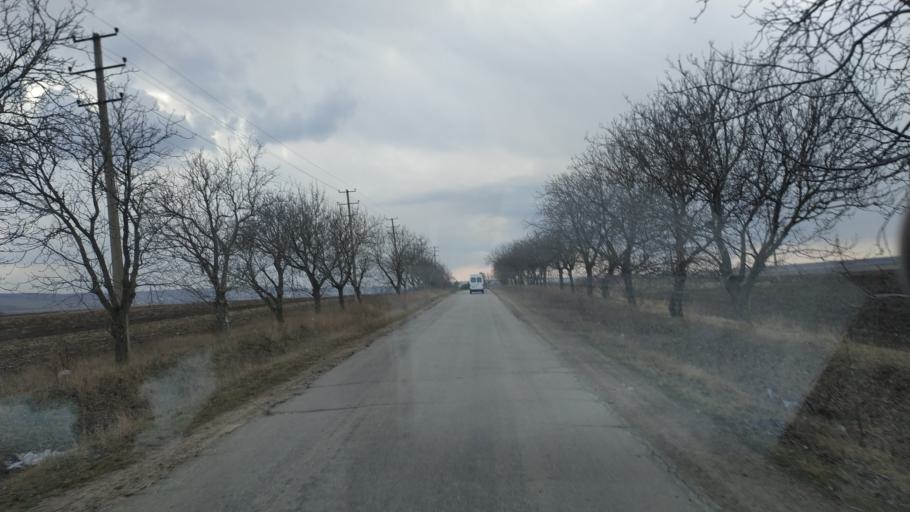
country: MD
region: Anenii Noi
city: Anenii Noi
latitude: 46.9111
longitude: 29.3269
